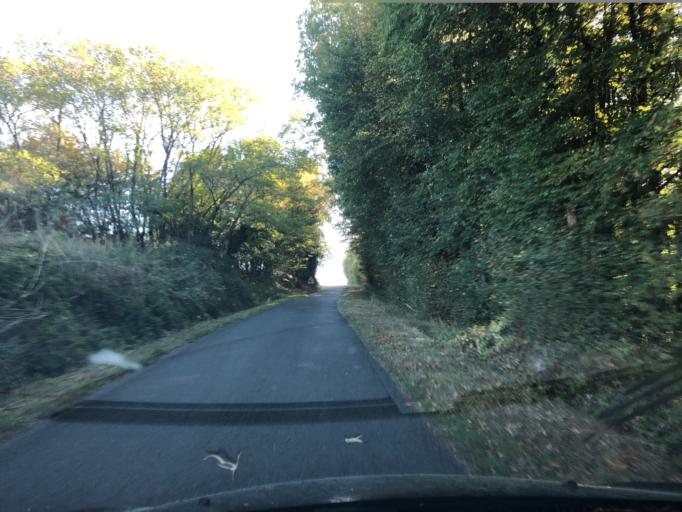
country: FR
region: Centre
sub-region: Departement d'Indre-et-Loire
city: Neuvy-le-Roi
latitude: 47.6546
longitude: 0.6110
